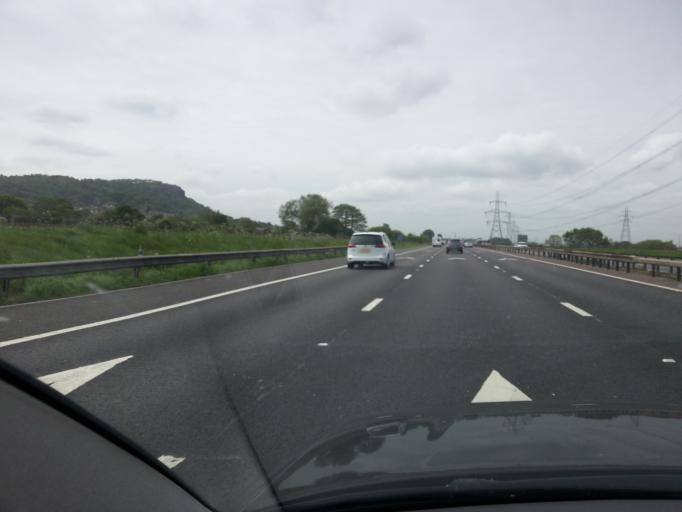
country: GB
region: England
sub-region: Cheshire West and Chester
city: Helsby
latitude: 53.2870
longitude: -2.7536
